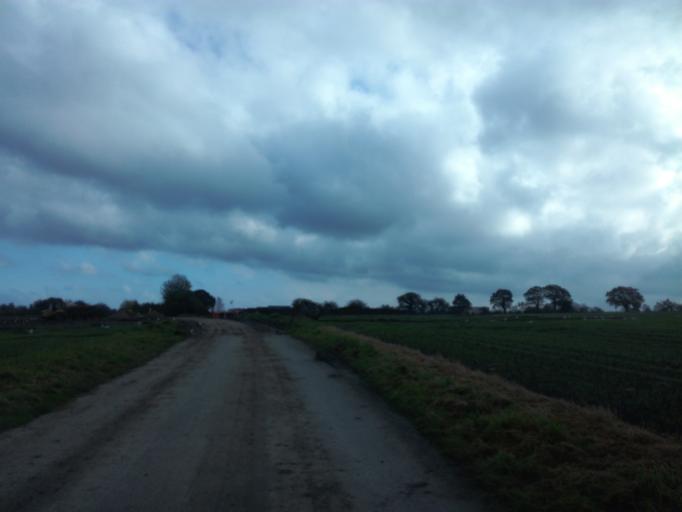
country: DK
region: South Denmark
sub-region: Vejle Kommune
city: Borkop
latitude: 55.6349
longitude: 9.6377
